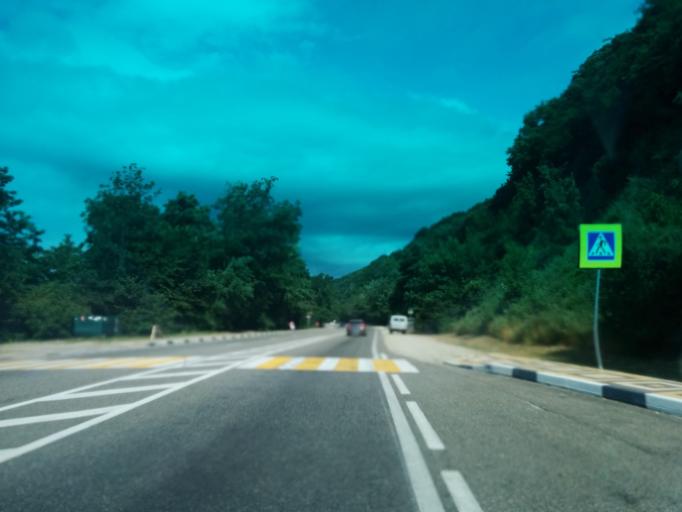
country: RU
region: Krasnodarskiy
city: Nebug
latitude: 44.1674
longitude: 38.9890
